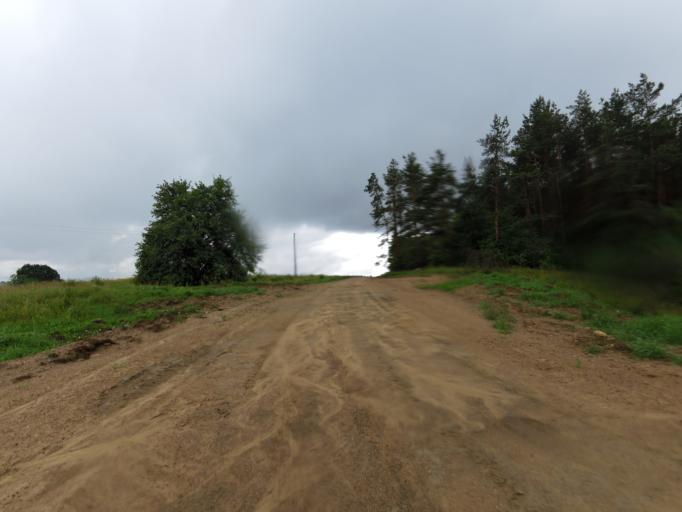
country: LT
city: Grigiskes
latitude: 54.7134
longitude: 25.1119
